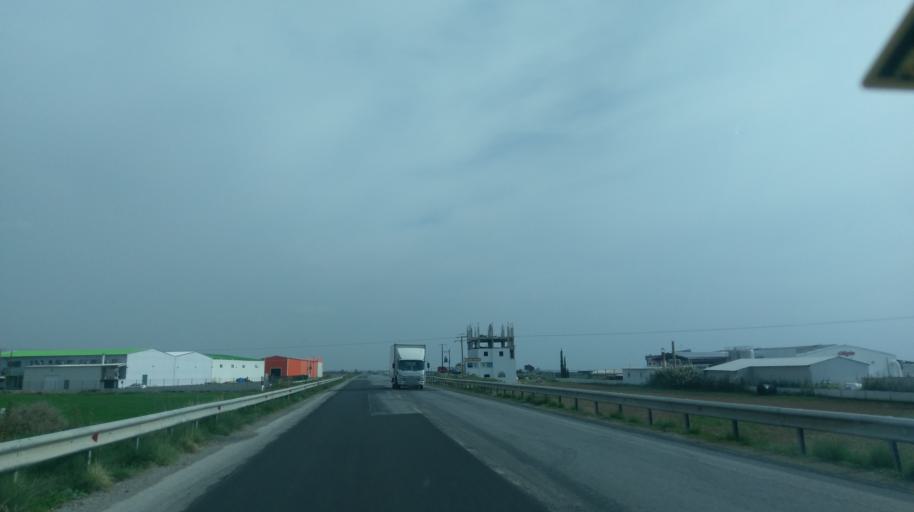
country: CY
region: Lefkosia
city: Geri
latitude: 35.2278
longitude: 33.5274
